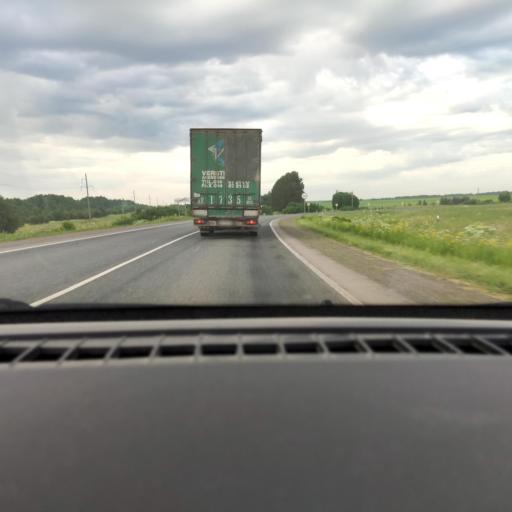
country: RU
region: Udmurtiya
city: Votkinsk
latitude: 57.3553
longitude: 54.4301
